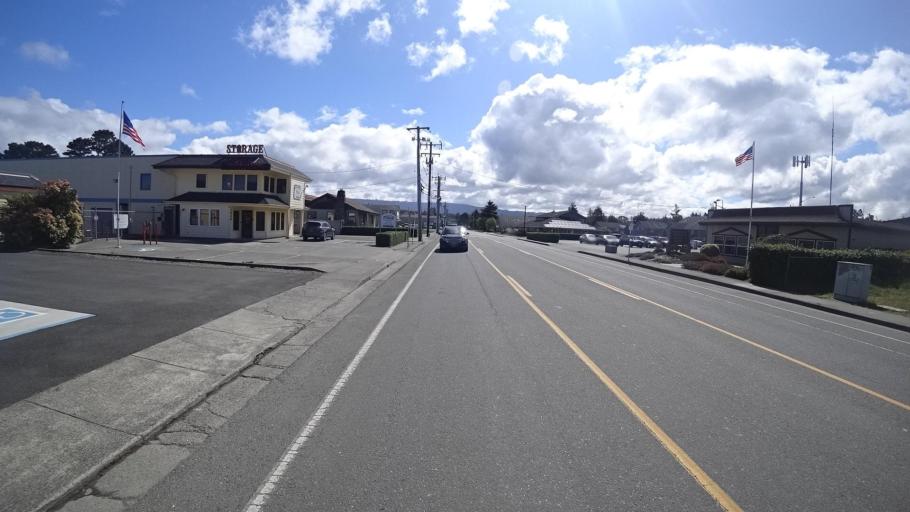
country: US
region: California
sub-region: Humboldt County
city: McKinleyville
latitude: 40.9361
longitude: -124.1002
